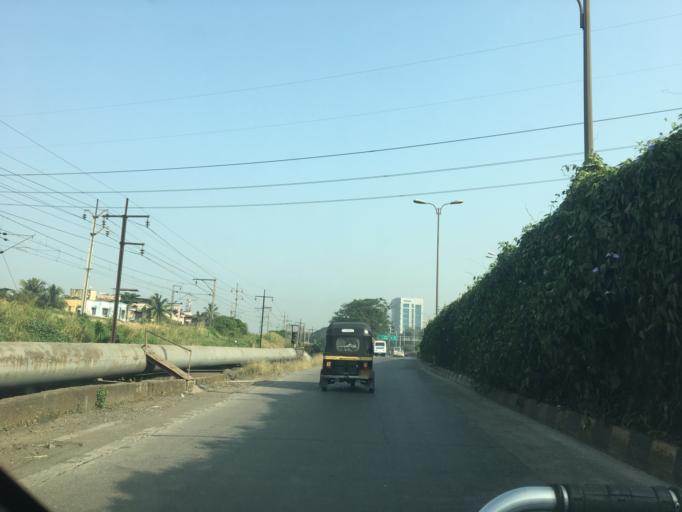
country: IN
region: Maharashtra
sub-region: Thane
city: Airoli
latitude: 19.1491
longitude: 73.0004
